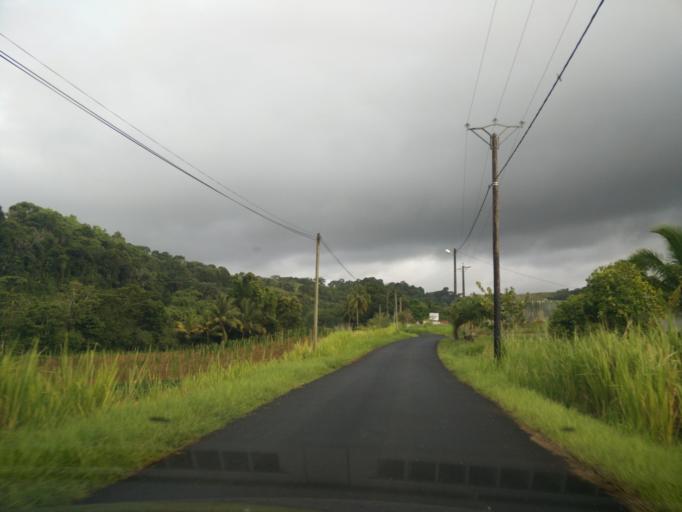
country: GP
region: Guadeloupe
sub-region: Guadeloupe
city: Petit-Bourg
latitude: 16.1695
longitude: -61.6231
